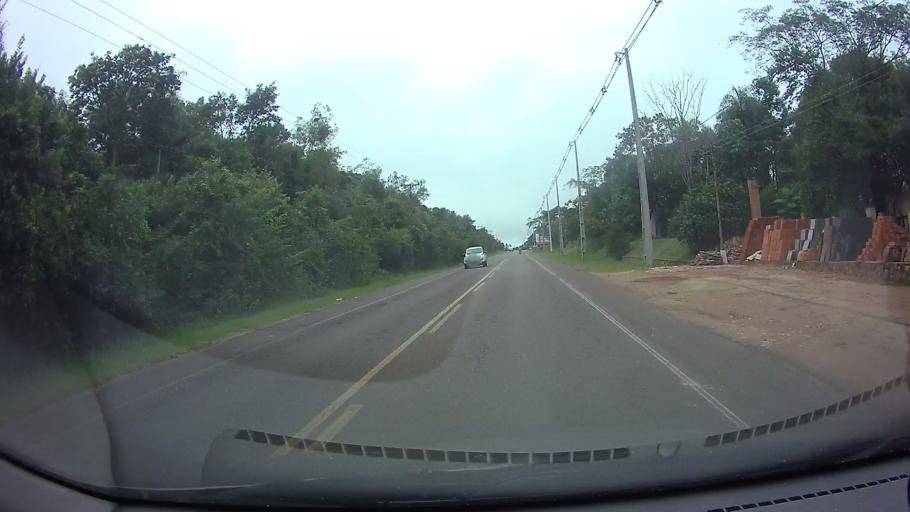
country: PY
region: Cordillera
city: Altos
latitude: -25.2786
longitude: -57.2612
